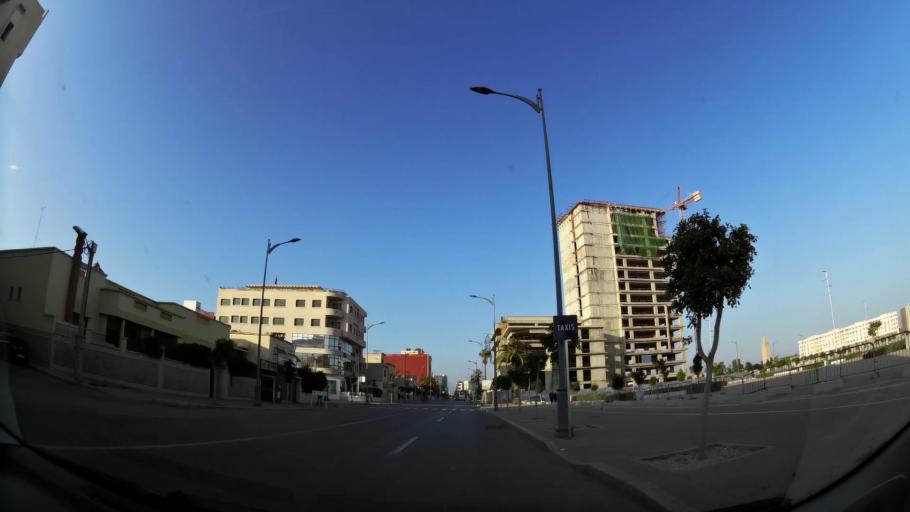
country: MA
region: Oriental
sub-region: Oujda-Angad
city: Oujda
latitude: 34.6788
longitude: -1.9236
